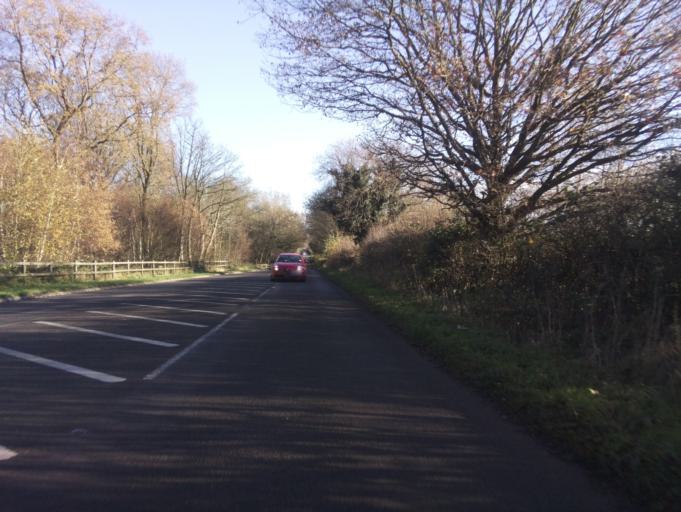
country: GB
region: England
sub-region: Staffordshire
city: Barton under Needwood
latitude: 52.8180
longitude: -1.7643
